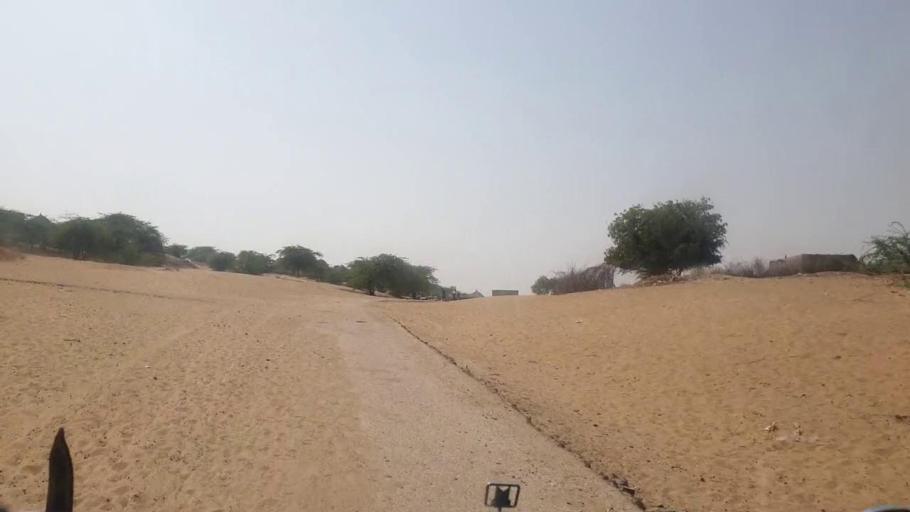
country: PK
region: Sindh
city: Islamkot
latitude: 25.1566
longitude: 70.2030
